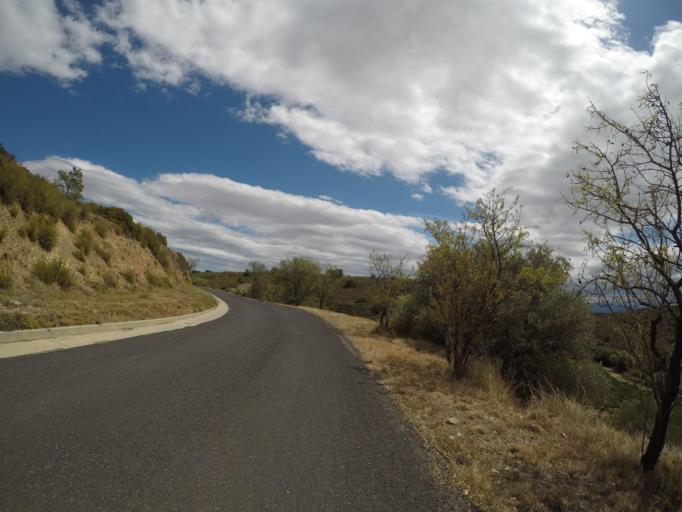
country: FR
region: Languedoc-Roussillon
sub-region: Departement des Pyrenees-Orientales
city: Baixas
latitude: 42.7552
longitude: 2.7675
